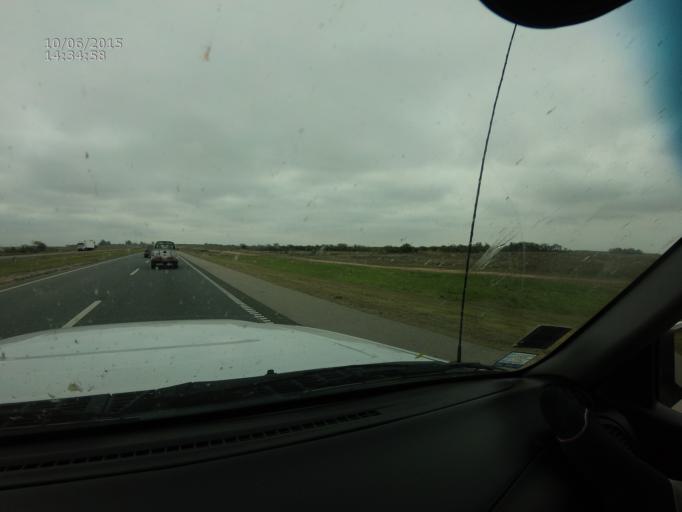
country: AR
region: Cordoba
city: James Craik
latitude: -32.1458
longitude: -63.4271
